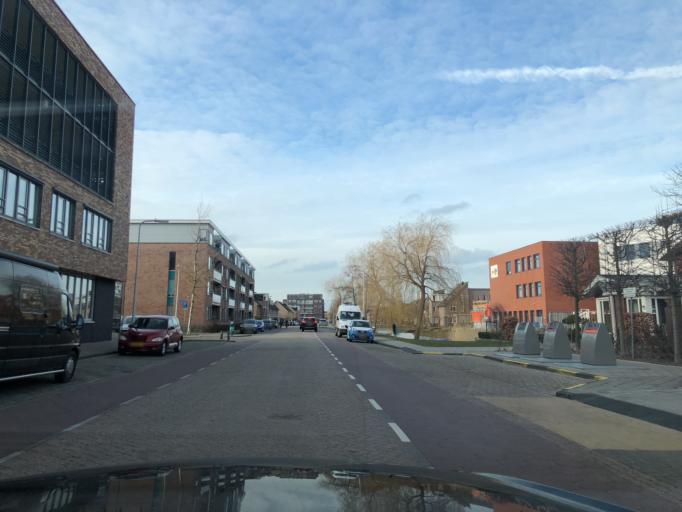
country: NL
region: South Holland
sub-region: Gemeente Westland
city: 's-Gravenzande
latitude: 52.0041
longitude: 4.1640
